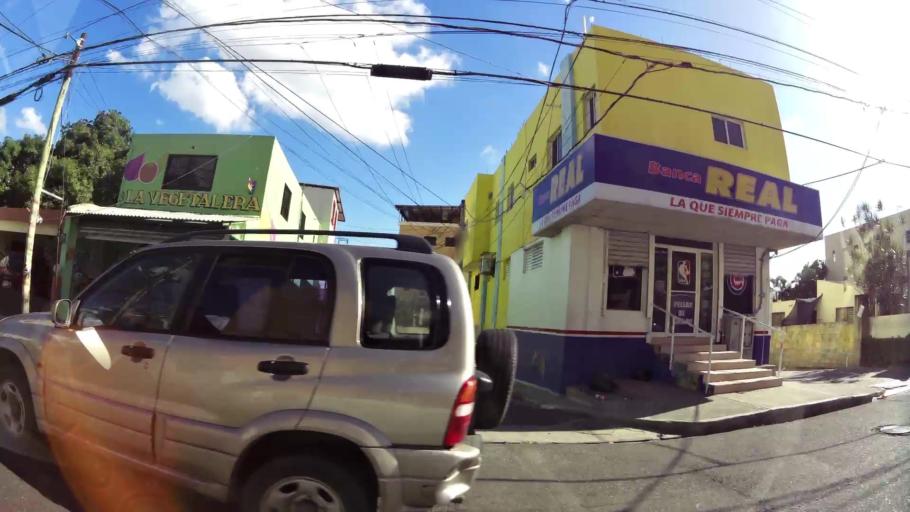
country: DO
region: Santiago
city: Santiago de los Caballeros
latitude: 19.4506
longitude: -70.6810
